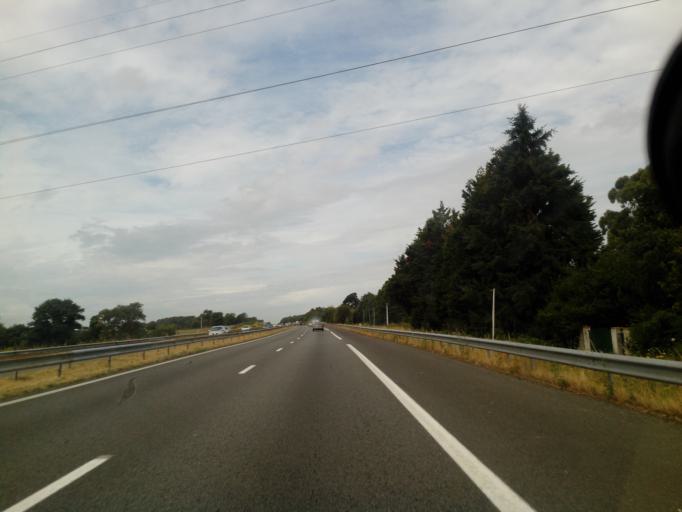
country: FR
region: Brittany
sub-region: Departement du Morbihan
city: Arradon
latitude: 47.6614
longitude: -2.8279
